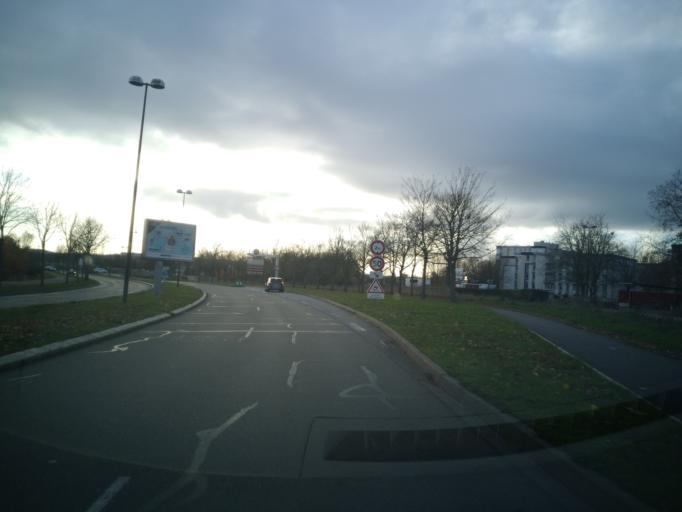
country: FR
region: Ile-de-France
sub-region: Departement des Yvelines
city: Guyancourt
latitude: 48.7730
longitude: 2.0836
